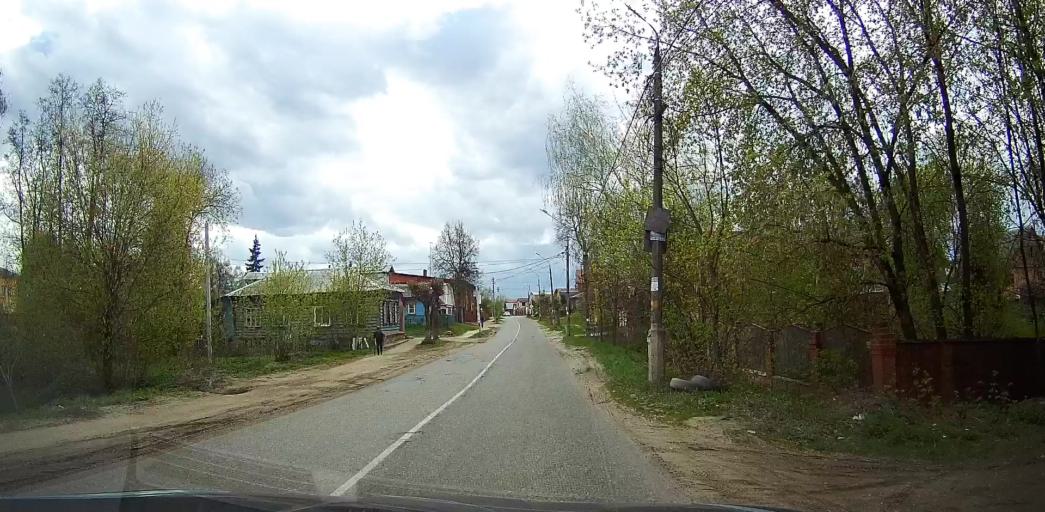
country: RU
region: Moskovskaya
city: Pavlovskiy Posad
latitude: 55.7796
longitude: 38.6454
